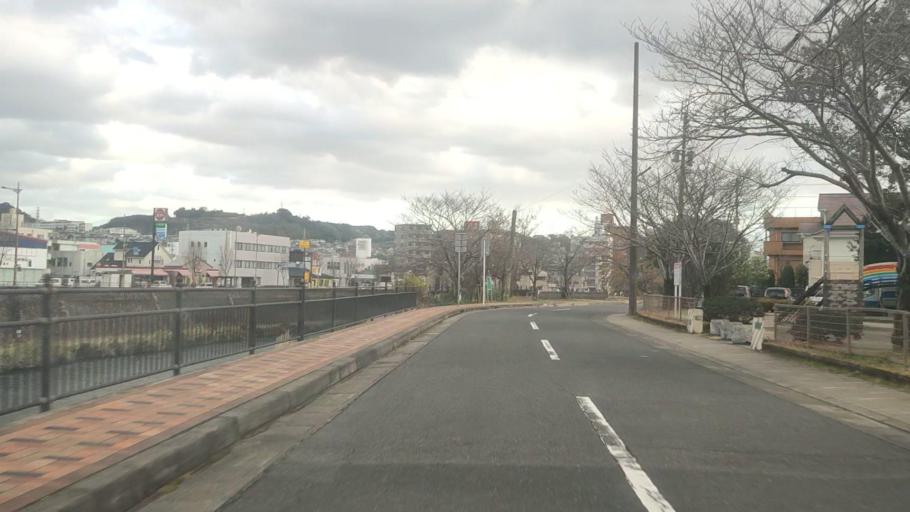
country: JP
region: Kagoshima
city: Kagoshima-shi
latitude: 31.6080
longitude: 130.5349
